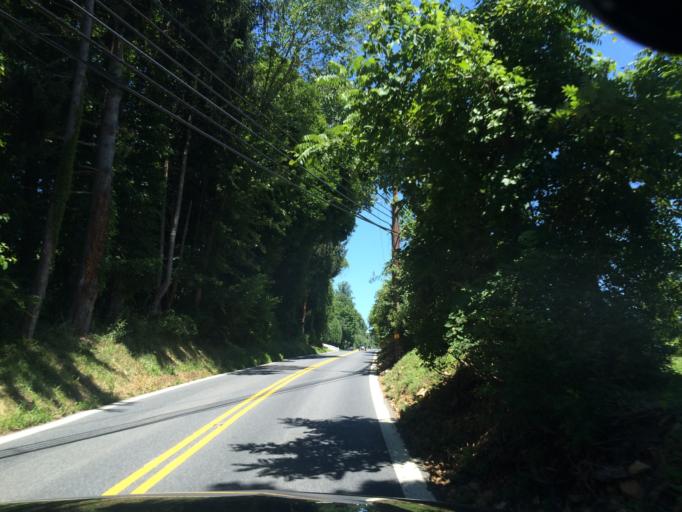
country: US
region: Maryland
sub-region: Baltimore County
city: Pikesville
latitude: 39.4231
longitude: -76.7086
